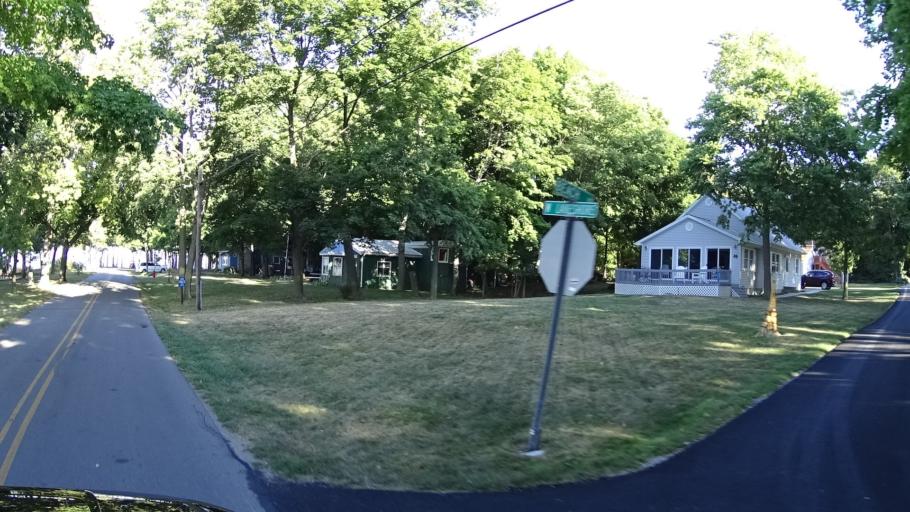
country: US
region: Ohio
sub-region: Erie County
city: Sandusky
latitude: 41.6002
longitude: -82.7324
